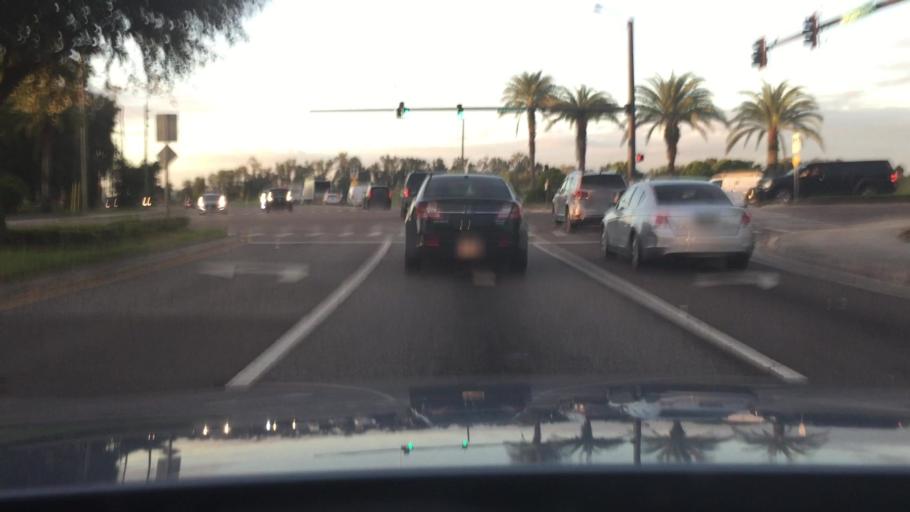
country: US
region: Florida
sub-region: Osceola County
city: Saint Cloud
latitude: 28.2492
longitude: -81.3175
